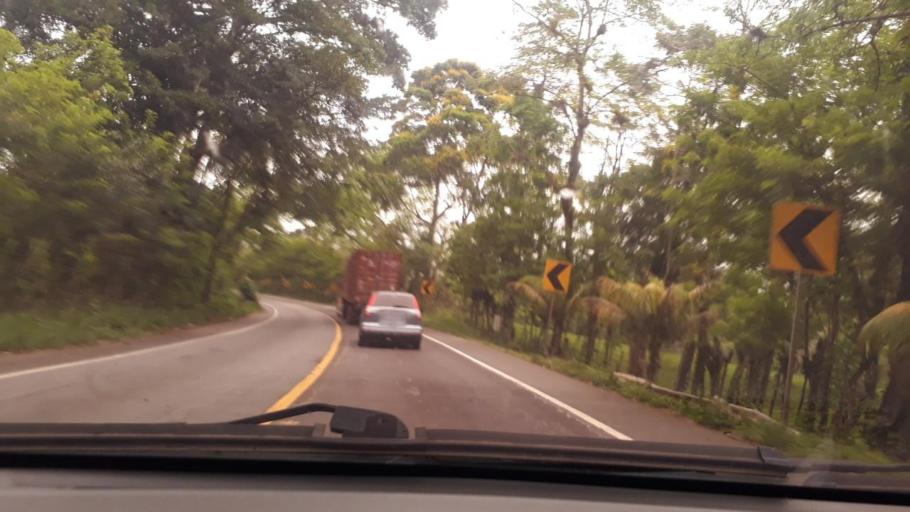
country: GT
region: Izabal
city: Morales
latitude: 15.5438
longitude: -88.7089
